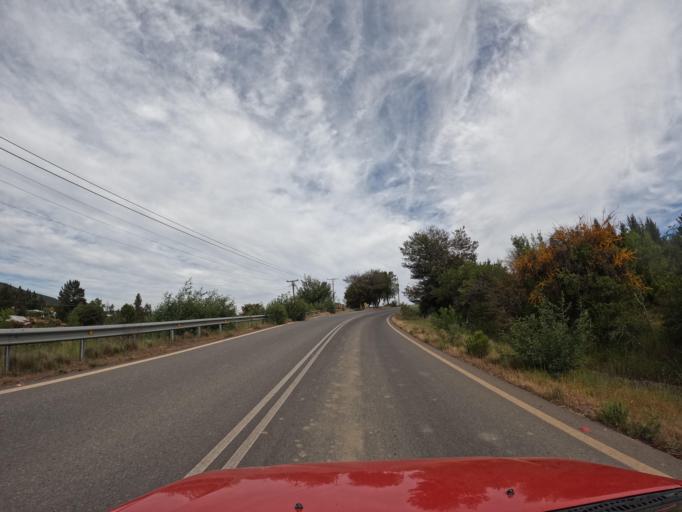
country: CL
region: Maule
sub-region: Provincia de Talca
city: Talca
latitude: -35.3235
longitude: -71.9315
